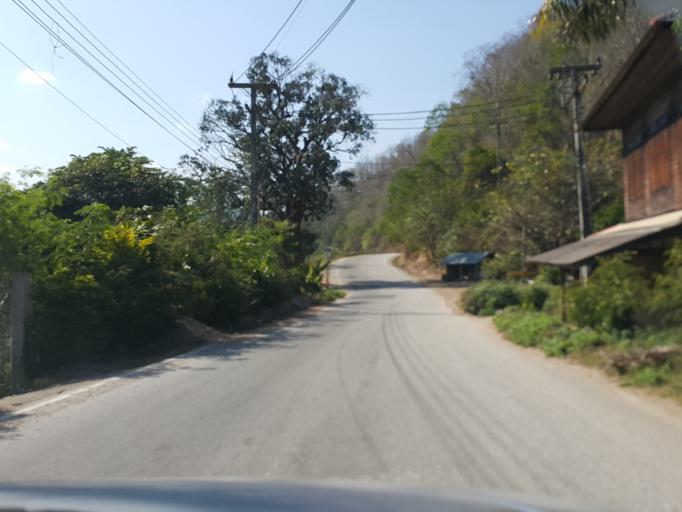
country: TH
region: Chiang Mai
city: Mae Wang
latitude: 18.6167
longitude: 98.7564
